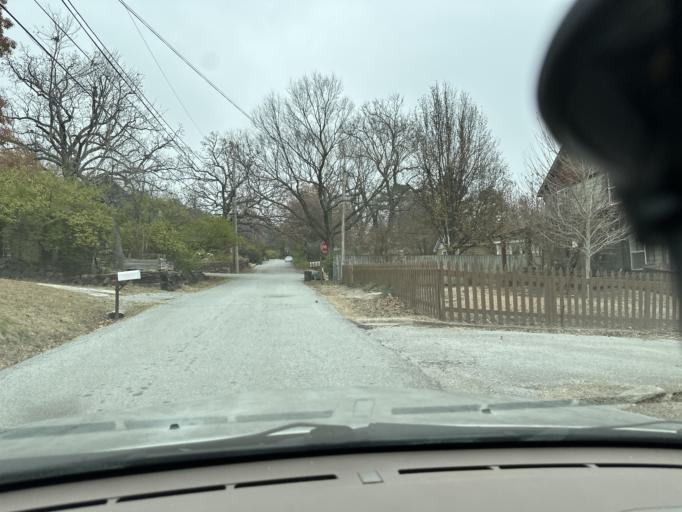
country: US
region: Arkansas
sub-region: Washington County
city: Fayetteville
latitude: 36.0752
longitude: -94.1550
